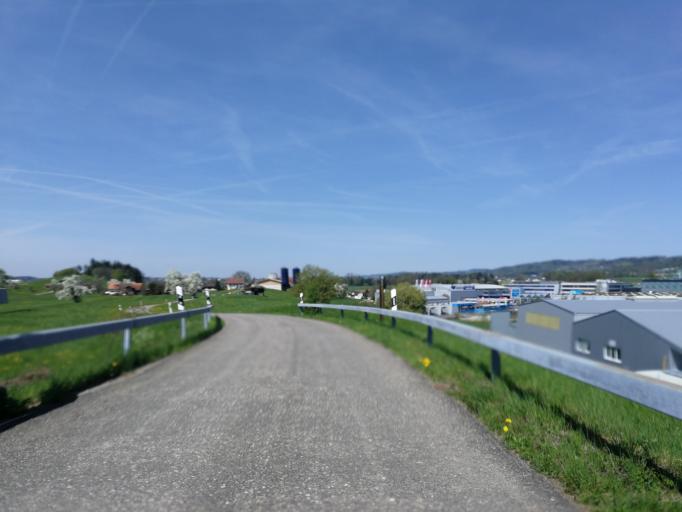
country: CH
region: Zurich
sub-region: Bezirk Hinwil
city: Wetzikon / Unter-Wetzikon
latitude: 47.3030
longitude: 8.8176
